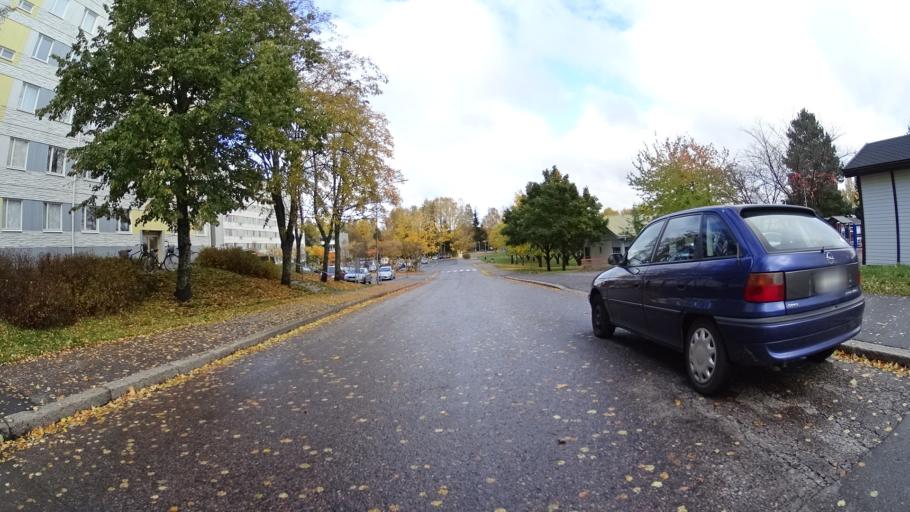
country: FI
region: Uusimaa
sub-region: Helsinki
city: Teekkarikylae
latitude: 60.2721
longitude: 24.8560
